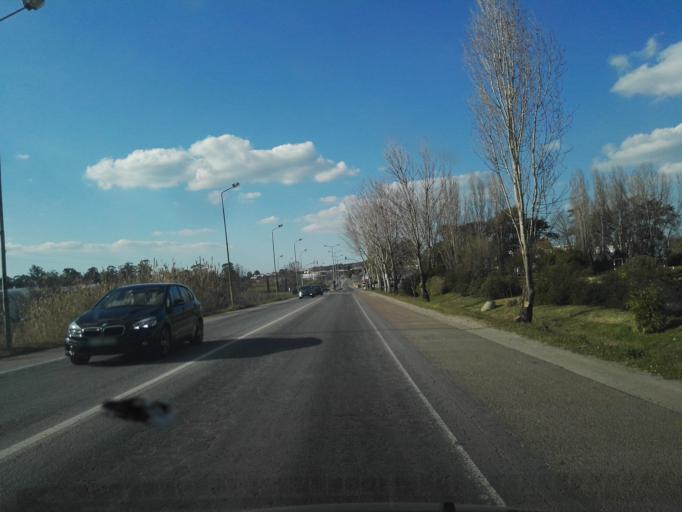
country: PT
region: Evora
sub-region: Evora
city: Evora
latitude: 38.5554
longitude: -7.9199
